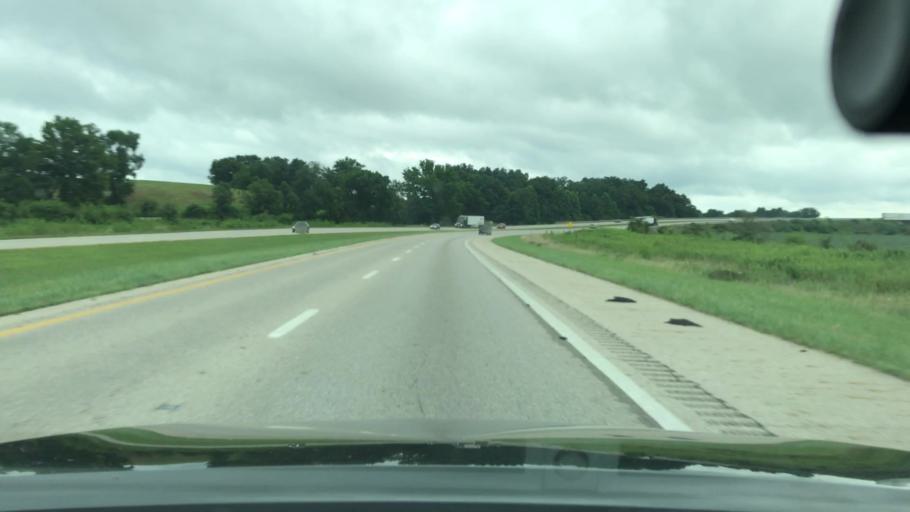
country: US
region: Ohio
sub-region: Ross County
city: Chillicothe
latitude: 39.2821
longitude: -82.8862
